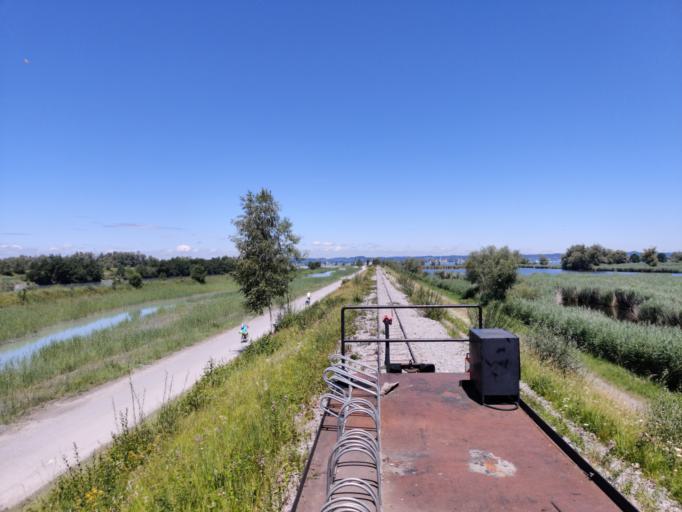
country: AT
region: Vorarlberg
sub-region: Politischer Bezirk Bregenz
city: Hard
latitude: 47.4914
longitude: 9.6719
